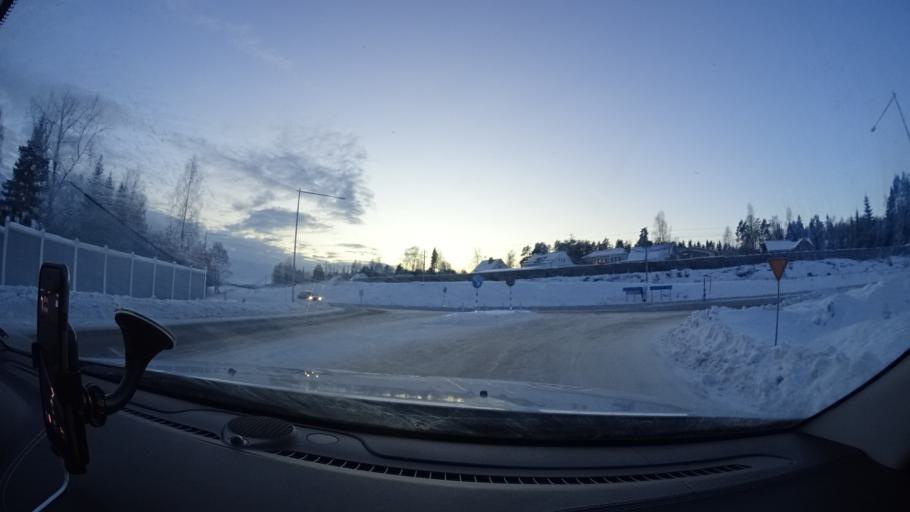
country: SE
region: Vaesternorrland
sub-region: Timra Kommun
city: Bergeforsen
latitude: 62.5276
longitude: 17.3872
